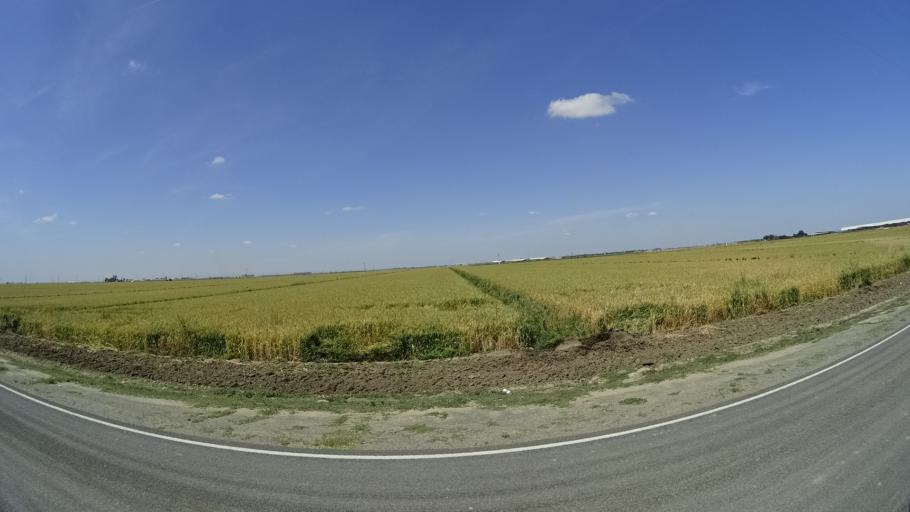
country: US
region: California
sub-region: Tulare County
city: Goshen
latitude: 36.3205
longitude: -119.4932
